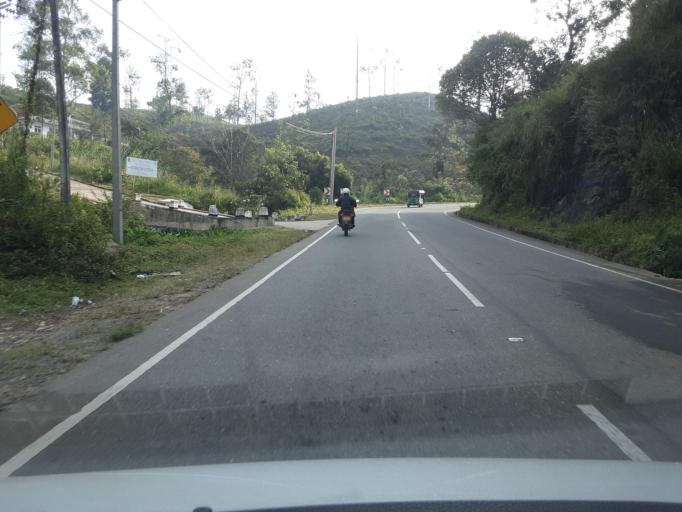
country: LK
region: Uva
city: Badulla
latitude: 6.9309
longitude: 80.9804
